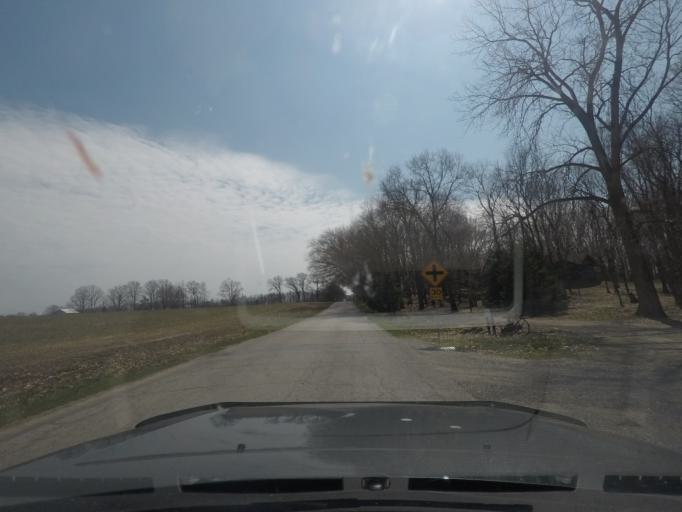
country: US
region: Indiana
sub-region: LaPorte County
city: Westville
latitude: 41.5343
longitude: -86.7989
